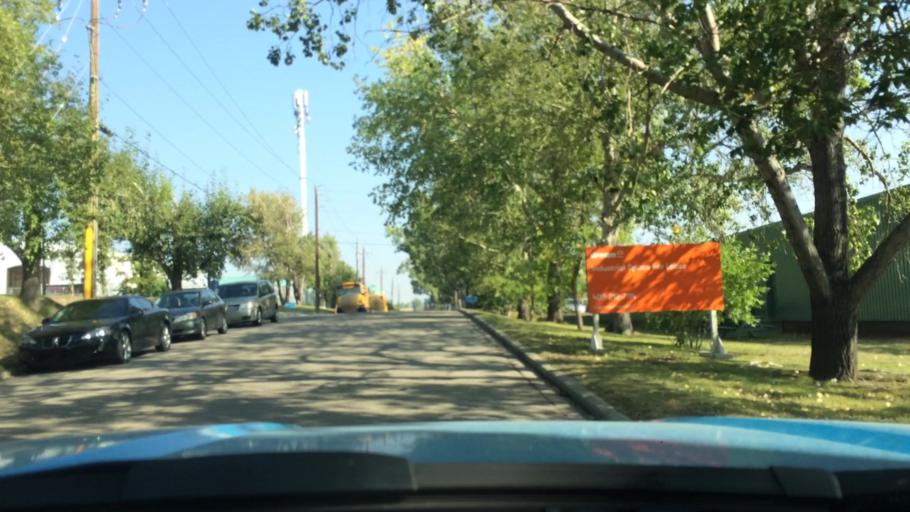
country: CA
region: Alberta
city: Calgary
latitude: 50.9903
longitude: -114.0509
